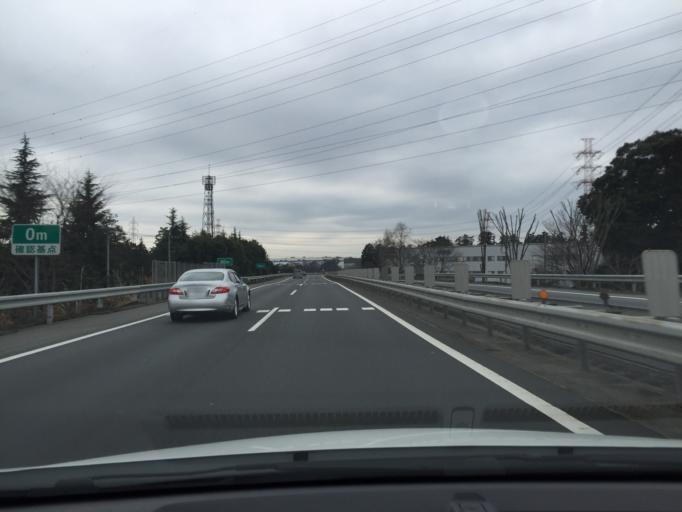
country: JP
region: Saitama
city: Sayama
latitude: 35.8907
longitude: 139.3878
